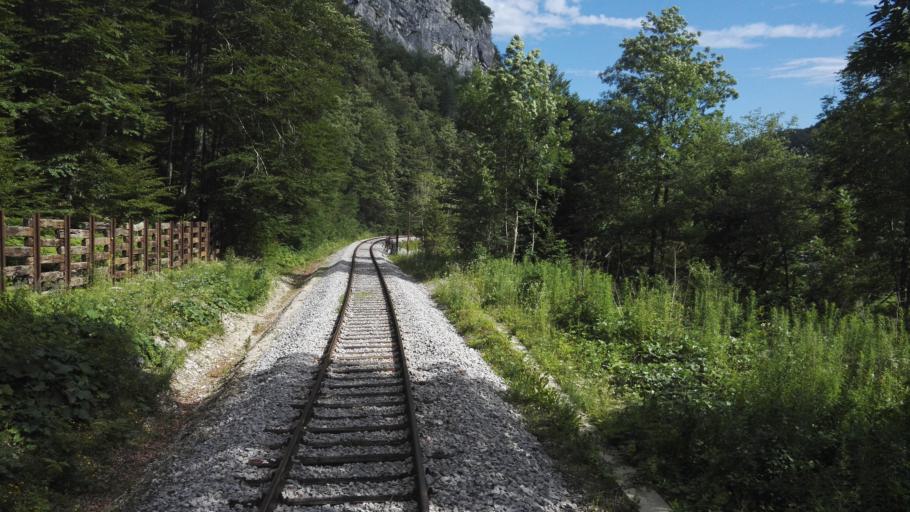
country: SI
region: Gorje
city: Zgornje Gorje
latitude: 46.3115
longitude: 14.0620
